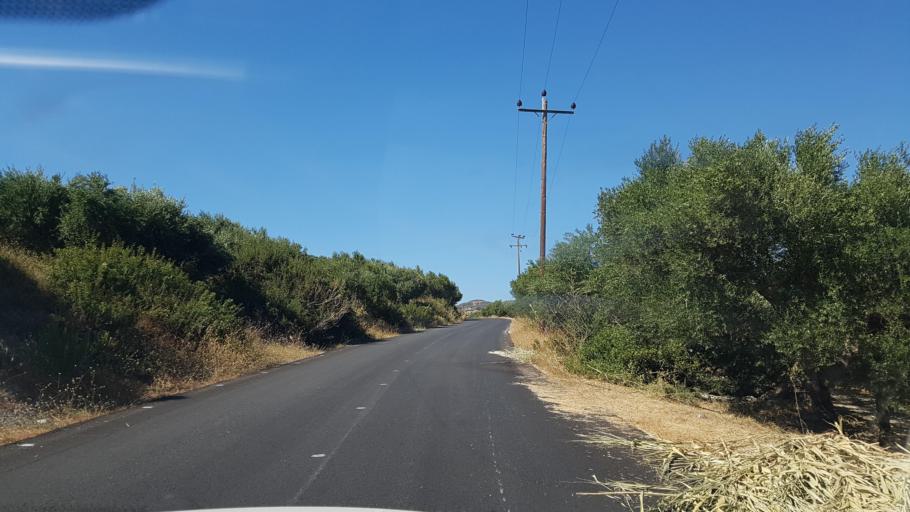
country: GR
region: Crete
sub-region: Nomos Chanias
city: Kissamos
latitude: 35.4989
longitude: 23.7222
